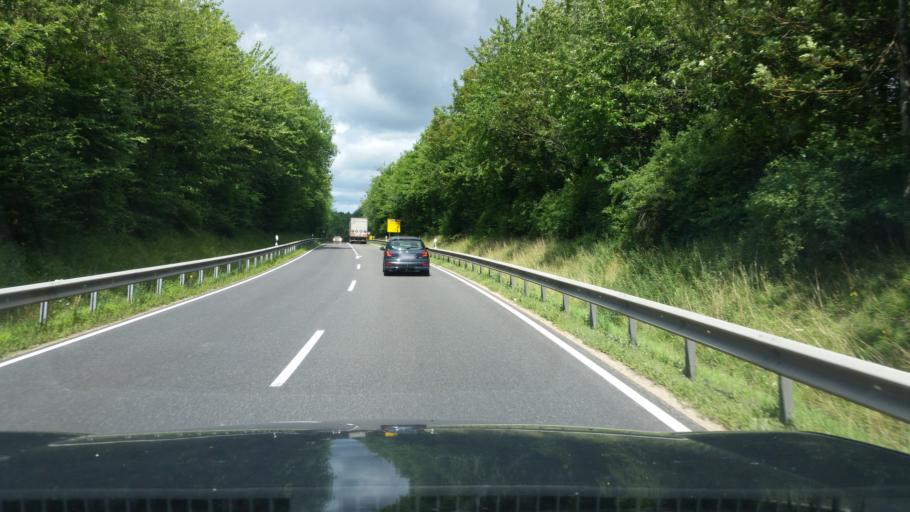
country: DE
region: Rheinland-Pfalz
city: Ohlenhard
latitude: 50.4480
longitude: 6.7104
